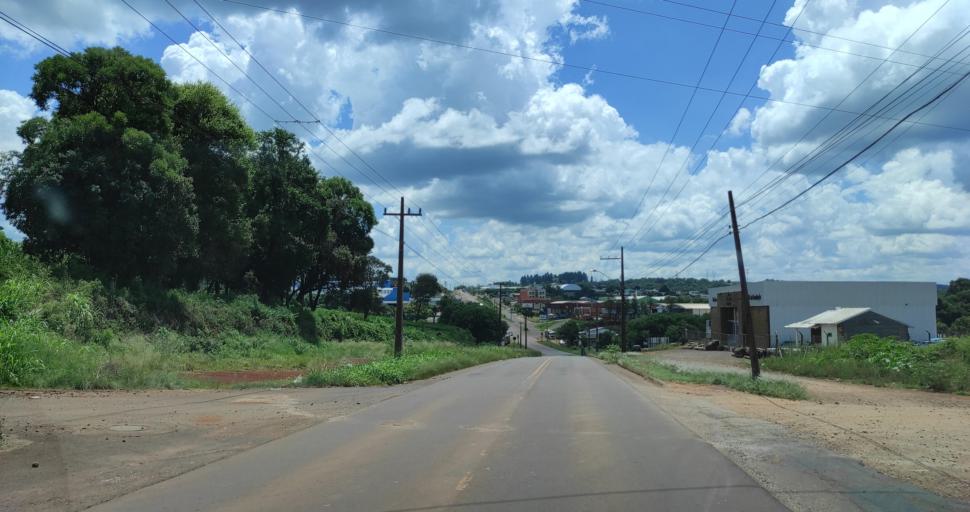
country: BR
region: Santa Catarina
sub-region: Xanxere
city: Xanxere
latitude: -26.8632
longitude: -52.4076
